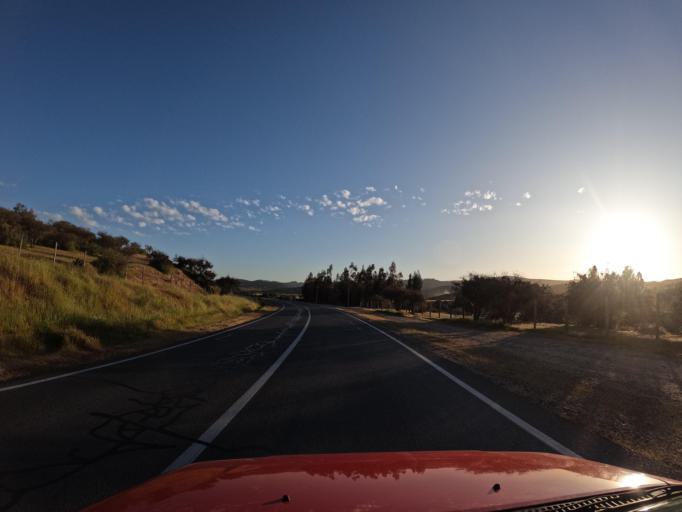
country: CL
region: O'Higgins
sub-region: Provincia de Colchagua
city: Santa Cruz
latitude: -34.3153
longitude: -71.7429
